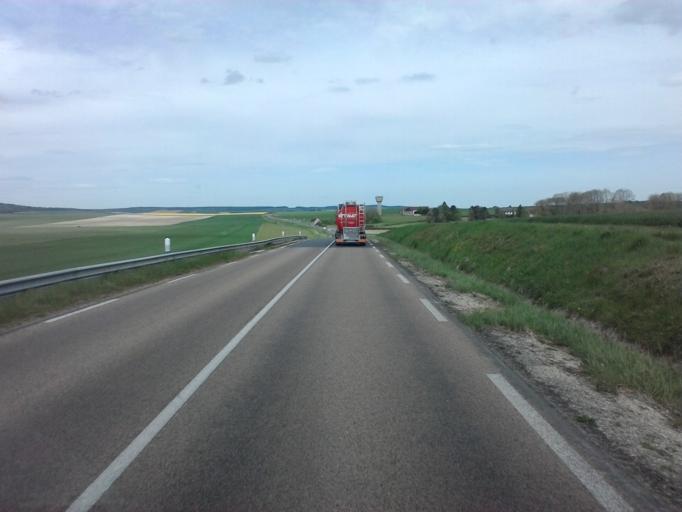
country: FR
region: Bourgogne
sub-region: Departement de l'Yonne
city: Neuvy-Sautour
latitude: 48.0620
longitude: 3.8059
